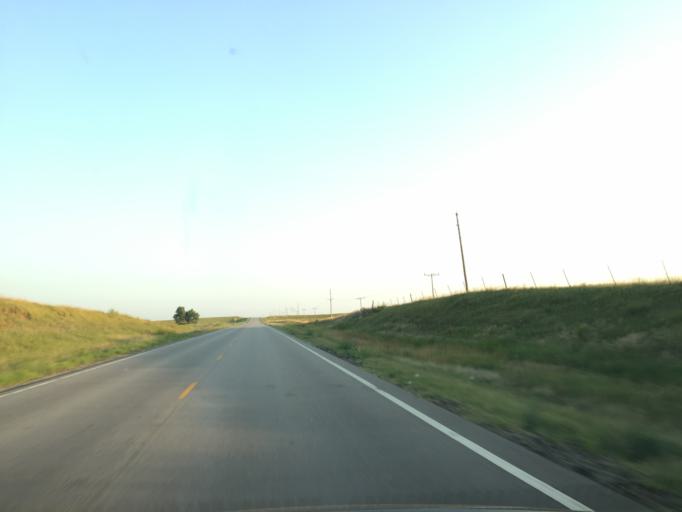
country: US
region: Kansas
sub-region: Ellsworth County
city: Ellsworth
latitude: 38.6611
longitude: -98.2021
